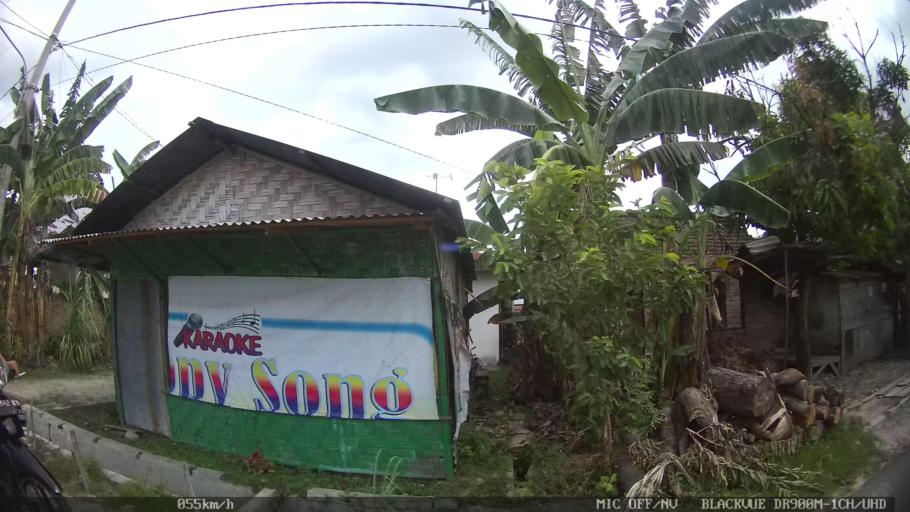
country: ID
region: North Sumatra
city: Percut
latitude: 3.5681
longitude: 98.8618
